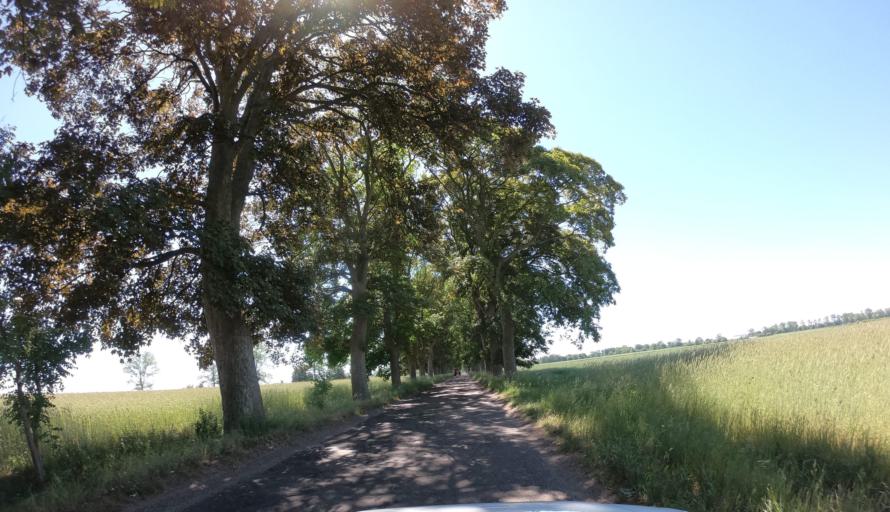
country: PL
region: West Pomeranian Voivodeship
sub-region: Powiat kamienski
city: Wolin
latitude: 53.9226
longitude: 14.6106
